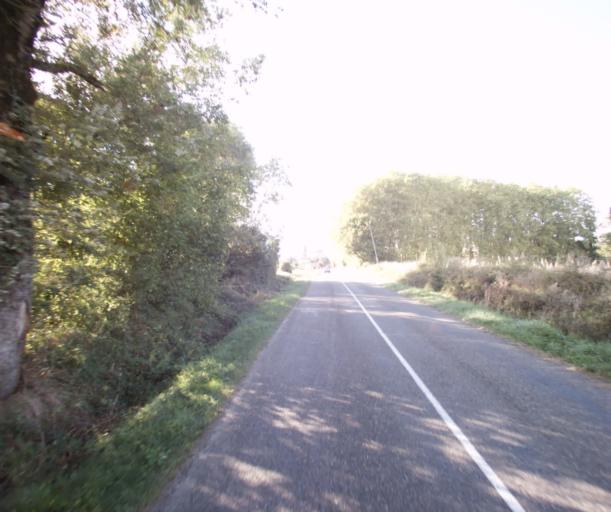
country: FR
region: Midi-Pyrenees
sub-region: Departement du Gers
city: Eauze
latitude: 43.8606
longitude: 0.0377
